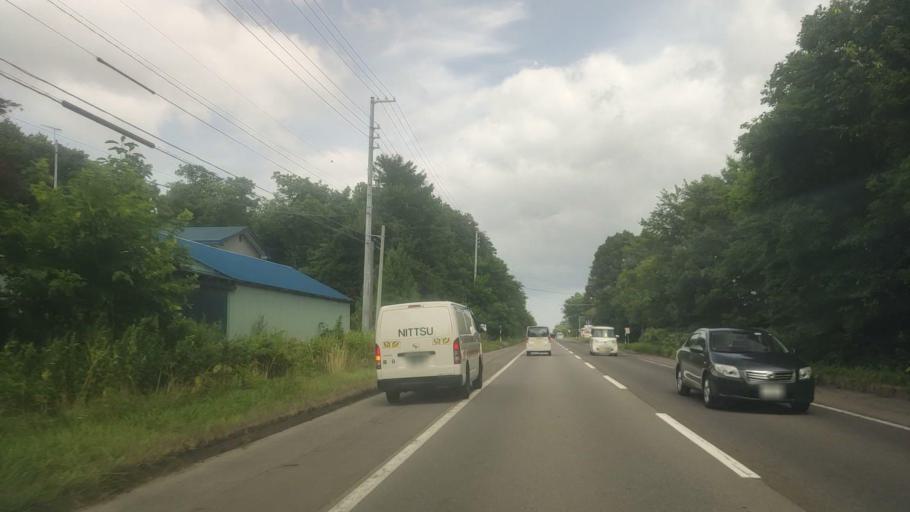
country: JP
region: Hokkaido
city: Nanae
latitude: 42.0469
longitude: 140.6019
